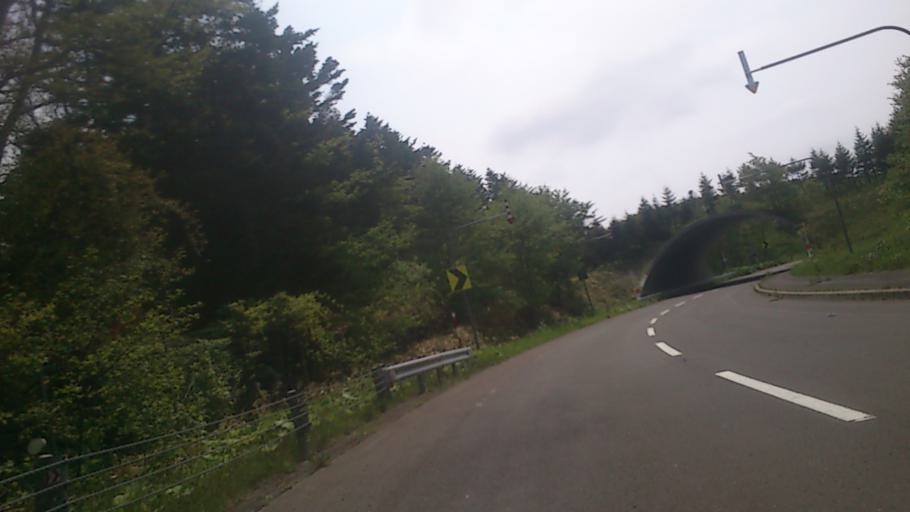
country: JP
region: Hokkaido
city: Nemuro
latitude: 43.2749
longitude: 145.5535
